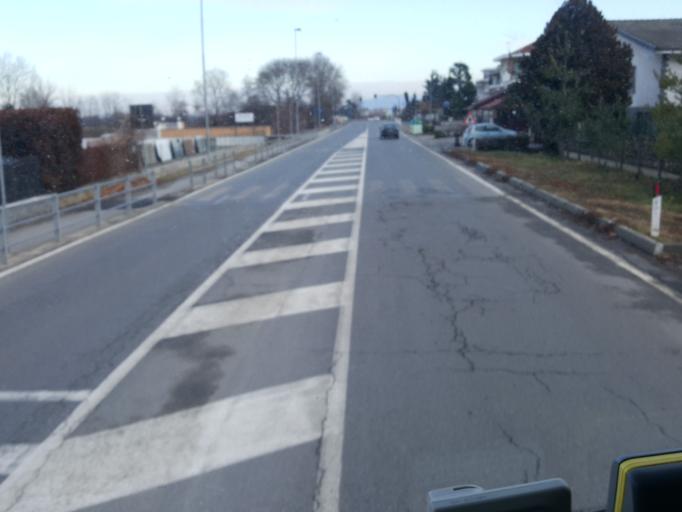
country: IT
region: Piedmont
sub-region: Provincia di Torino
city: Druento
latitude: 45.1386
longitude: 7.5743
